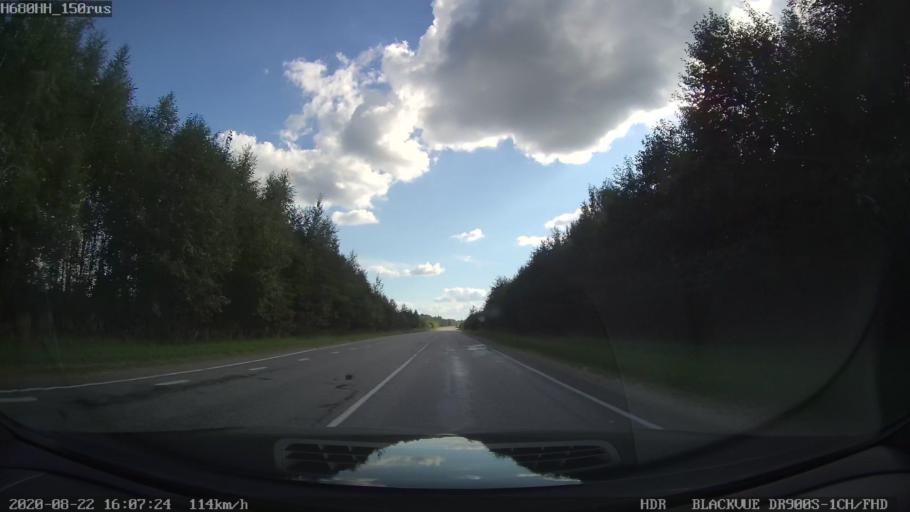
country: RU
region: Tverskaya
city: Rameshki
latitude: 57.5534
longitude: 36.3139
